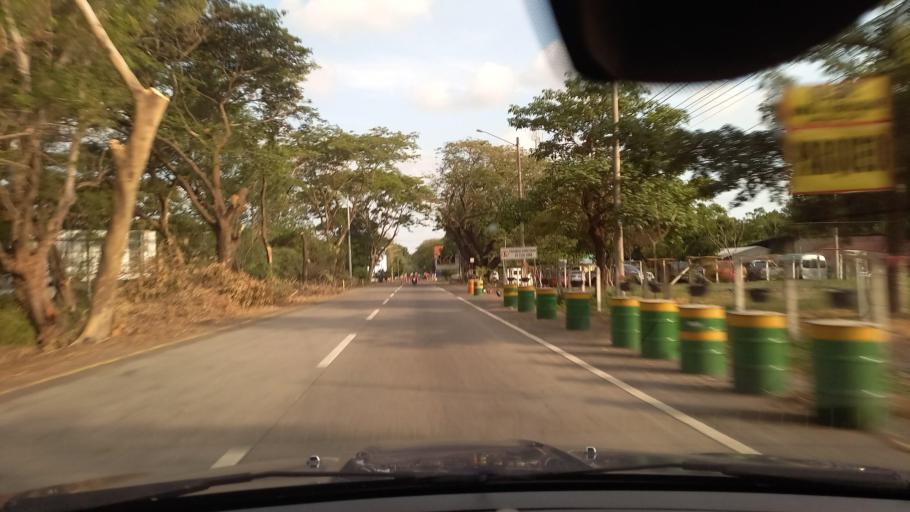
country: SV
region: La Paz
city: El Rosario
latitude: 13.4569
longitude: -89.0617
